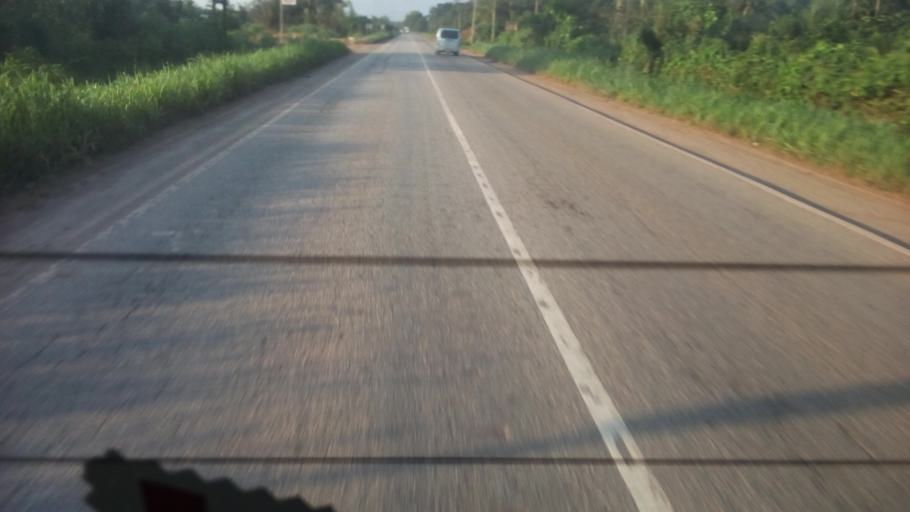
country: GH
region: Western
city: Tarkwa
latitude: 5.1891
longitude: -2.0368
